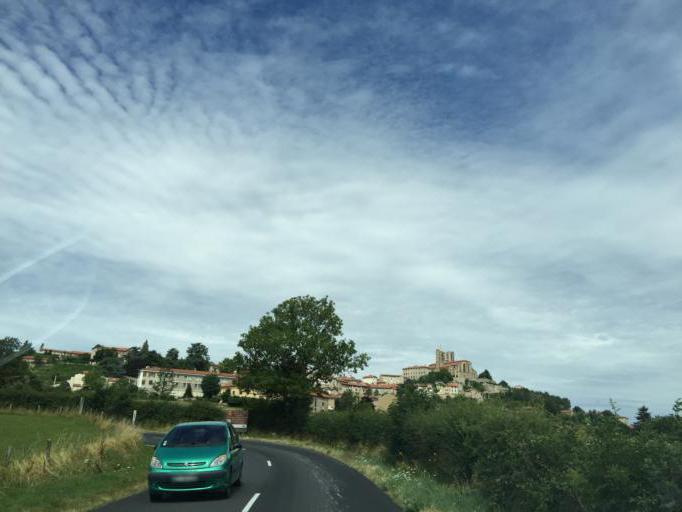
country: FR
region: Rhone-Alpes
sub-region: Departement de la Loire
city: Saint-Bonnet-le-Chateau
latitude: 45.4197
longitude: 4.0722
